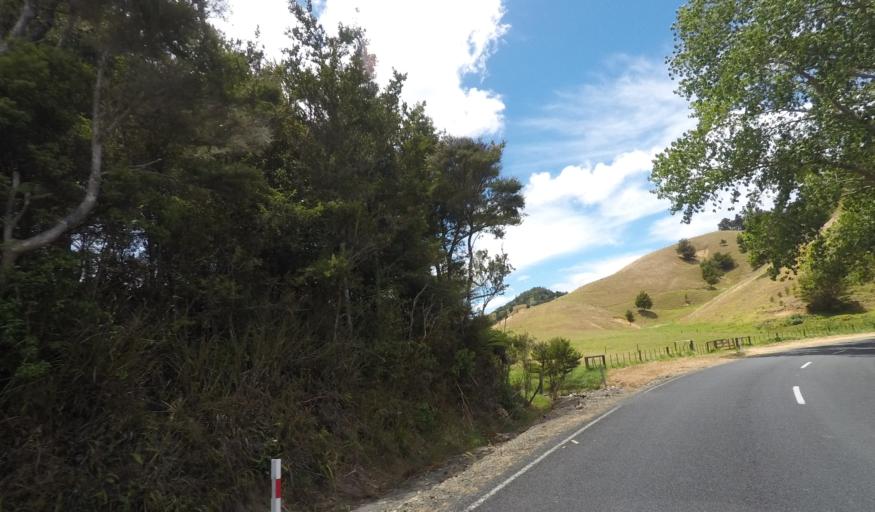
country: NZ
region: Northland
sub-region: Whangarei
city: Ngunguru
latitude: -35.5061
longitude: 174.4398
